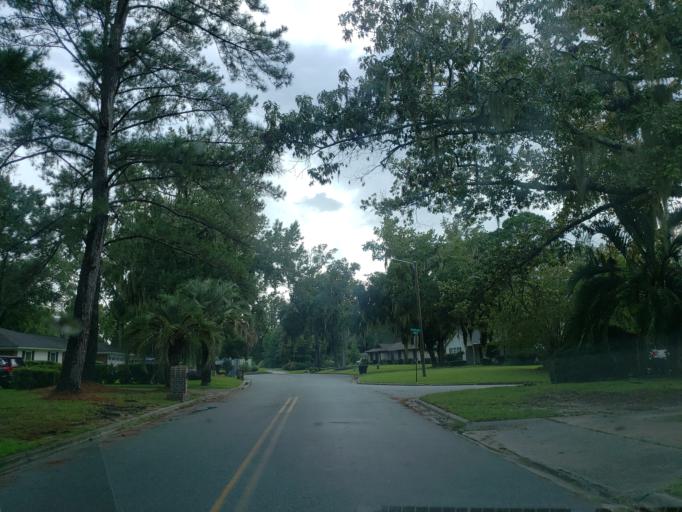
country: US
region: Georgia
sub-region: Chatham County
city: Georgetown
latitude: 31.9820
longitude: -81.2263
